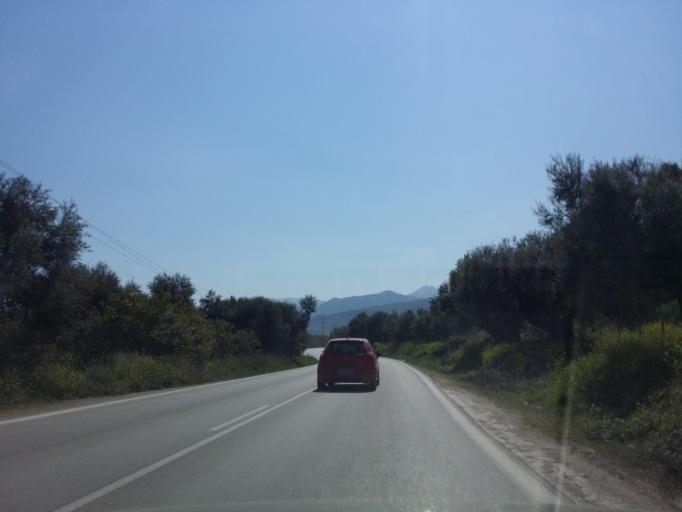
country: GR
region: West Greece
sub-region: Nomos Achaias
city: Siliveniotika
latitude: 38.1659
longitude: 22.3330
